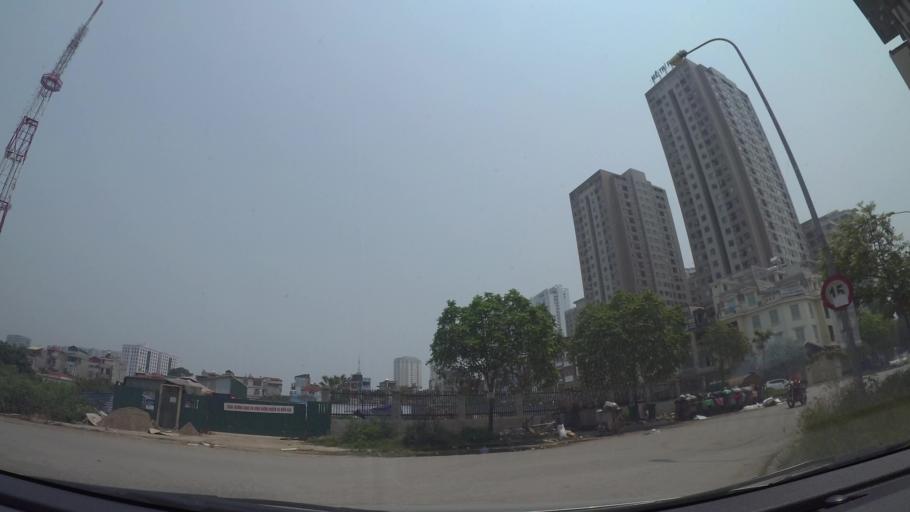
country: VN
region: Ha Noi
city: Thanh Xuan
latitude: 20.9975
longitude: 105.7842
